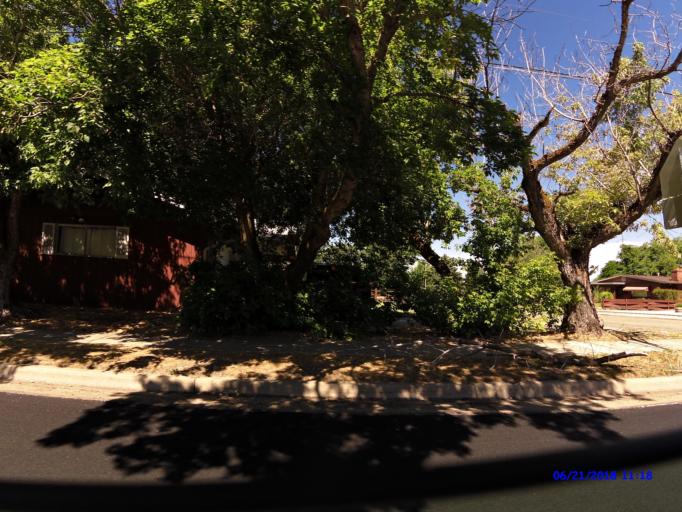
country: US
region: Utah
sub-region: Weber County
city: Ogden
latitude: 41.2498
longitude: -111.9547
